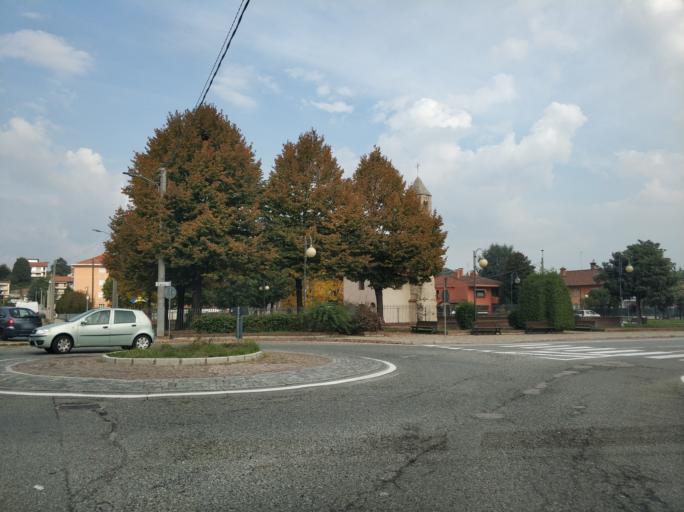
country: IT
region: Piedmont
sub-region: Provincia di Torino
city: San Carlo Canavese
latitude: 45.2401
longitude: 7.6067
